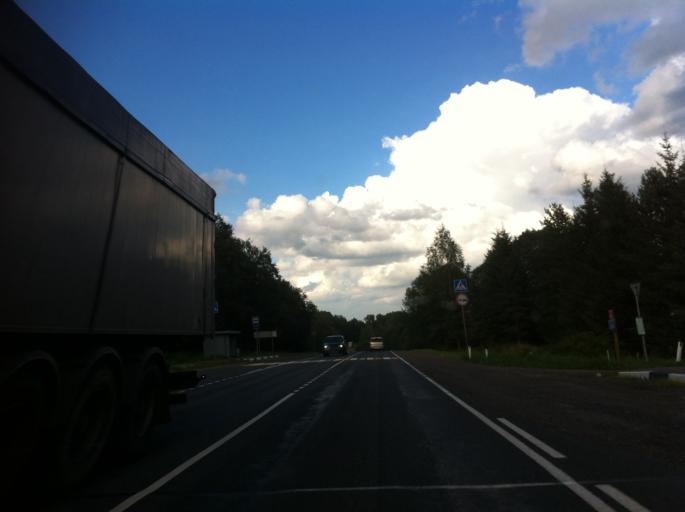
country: RU
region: Pskov
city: Strugi-Krasnyye
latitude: 58.1918
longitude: 29.2791
